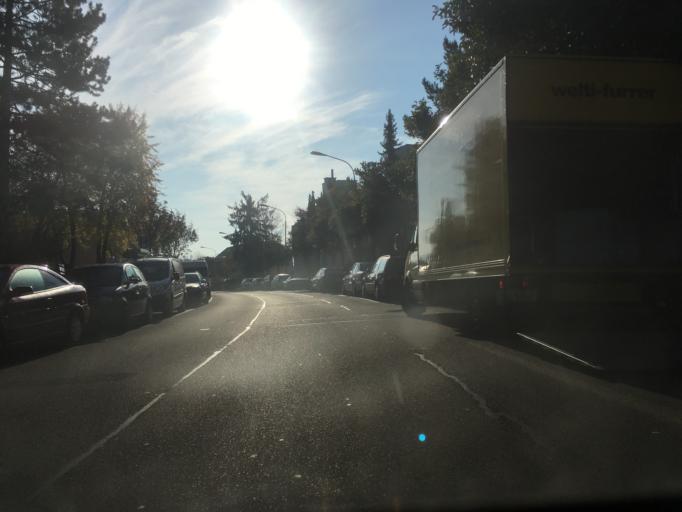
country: CH
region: Zurich
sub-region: Bezirk Zuerich
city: Zuerich (Kreis 10) / Hoengg
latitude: 47.4010
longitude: 8.4997
